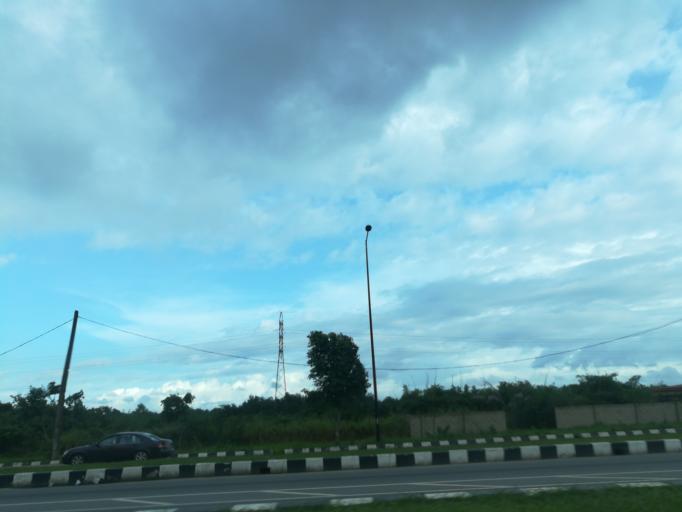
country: NG
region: Lagos
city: Ebute Ikorodu
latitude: 6.6148
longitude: 3.4434
